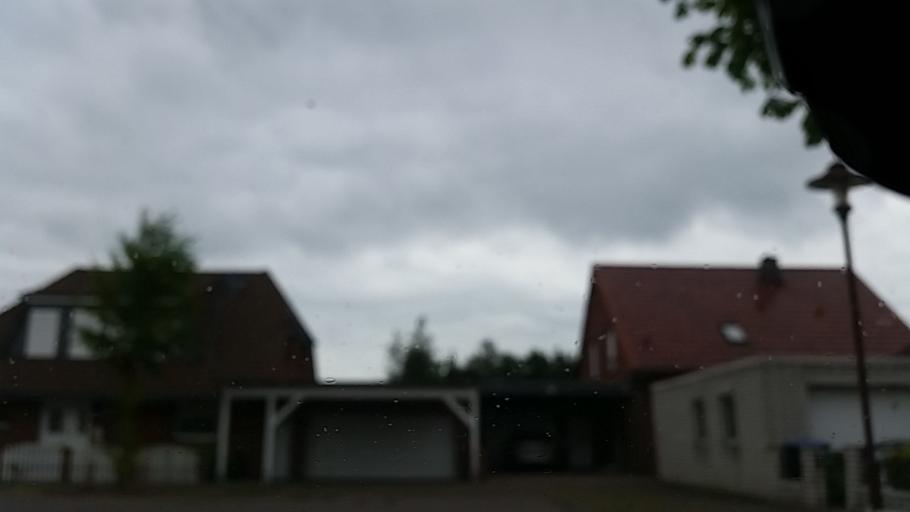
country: DE
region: Lower Saxony
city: Wolfsburg
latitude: 52.4133
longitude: 10.8463
